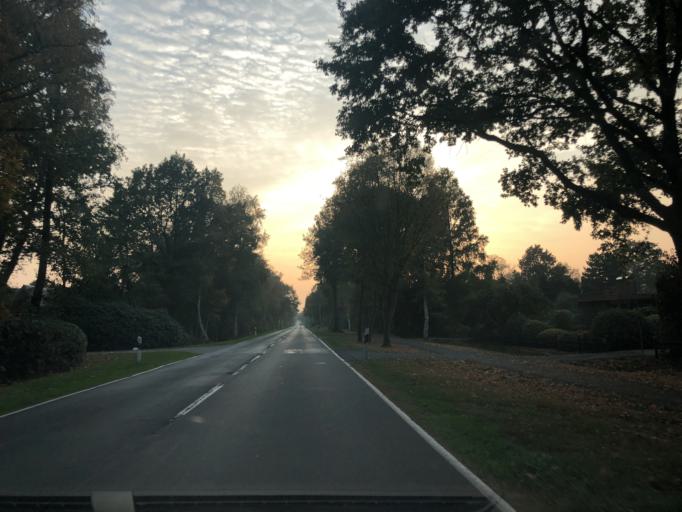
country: DE
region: Lower Saxony
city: Wardenburg
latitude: 53.0336
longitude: 8.0972
